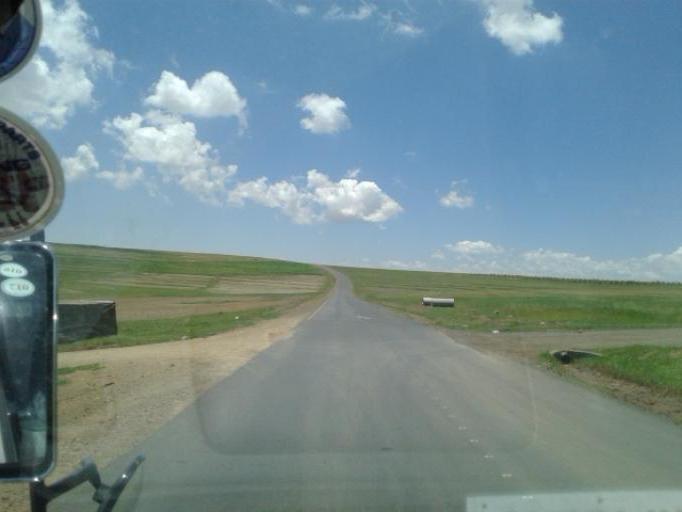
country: LS
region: Maseru
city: Maseru
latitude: -29.3072
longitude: 27.6045
